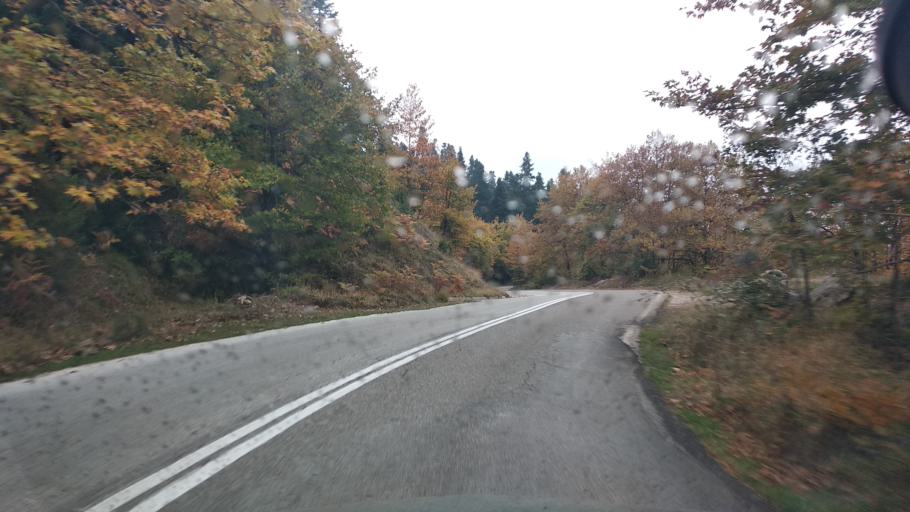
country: GR
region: Thessaly
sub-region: Trikala
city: Pyli
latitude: 39.5173
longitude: 21.5256
